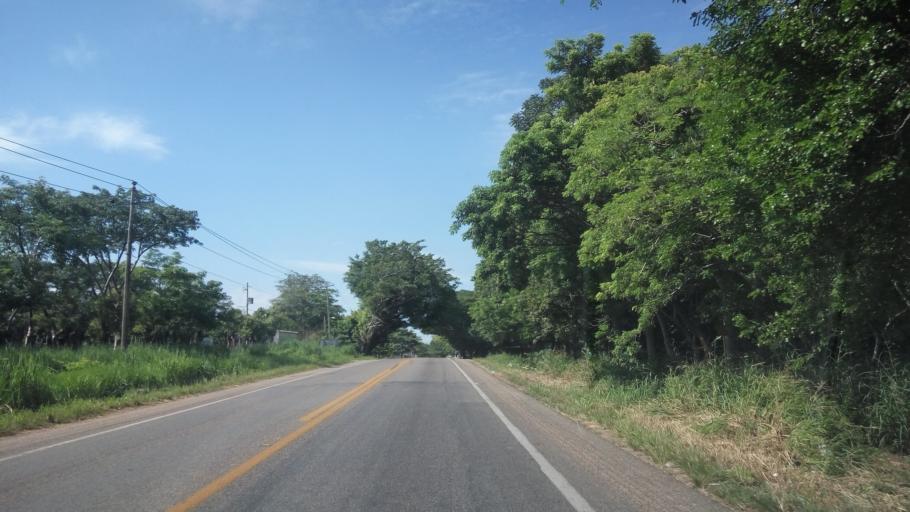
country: MX
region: Tabasco
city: Rio de Teapa
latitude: 17.8069
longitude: -92.9364
